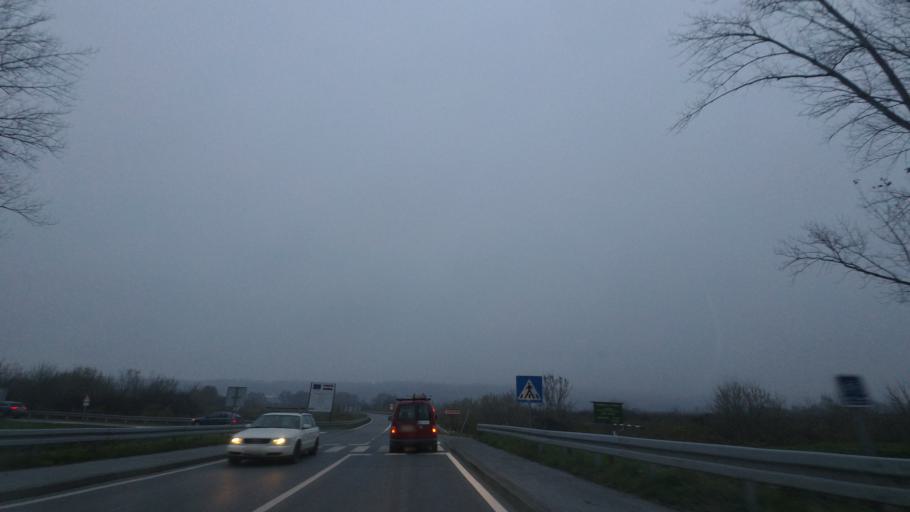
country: HR
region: Sisacko-Moslavacka
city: Petrinja
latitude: 45.4476
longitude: 16.2597
